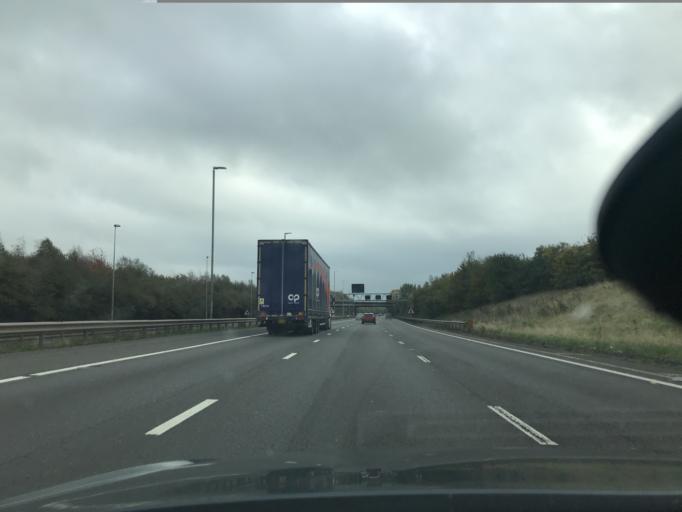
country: GB
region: England
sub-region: Warwickshire
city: Water Orton
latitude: 52.4980
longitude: -1.7176
